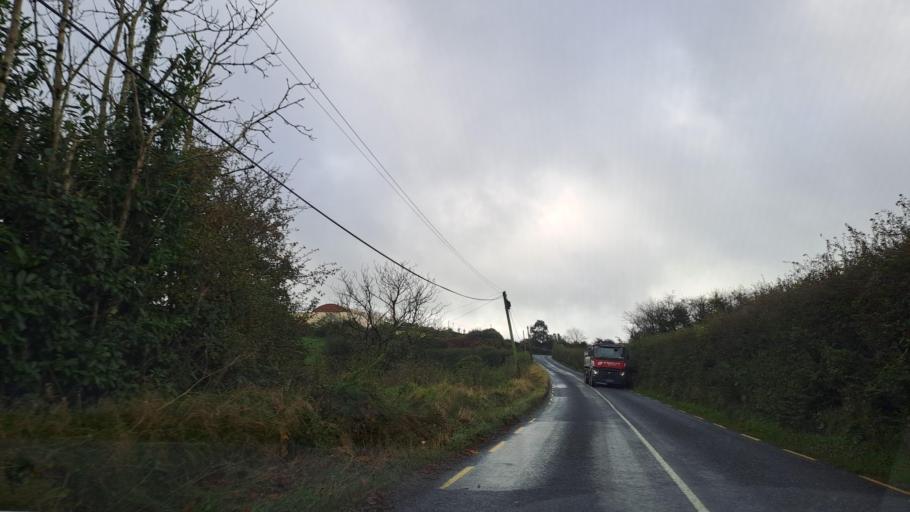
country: IE
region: Ulster
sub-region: An Cabhan
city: Bailieborough
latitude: 53.8960
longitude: -7.0130
